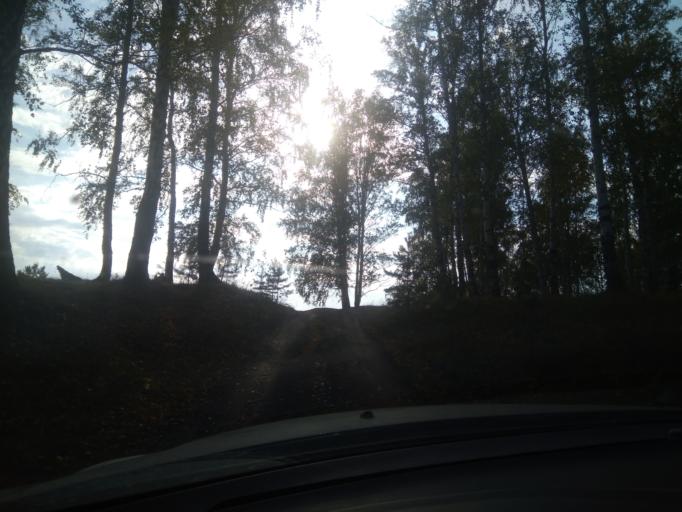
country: RU
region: Sverdlovsk
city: Pokrovskoye
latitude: 56.4273
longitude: 61.6152
